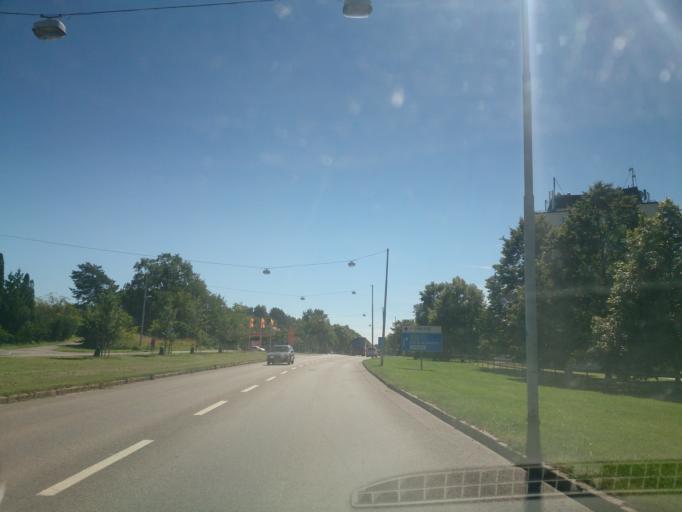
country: SE
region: OEstergoetland
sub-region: Linkopings Kommun
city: Linkoping
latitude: 58.3945
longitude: 15.6440
